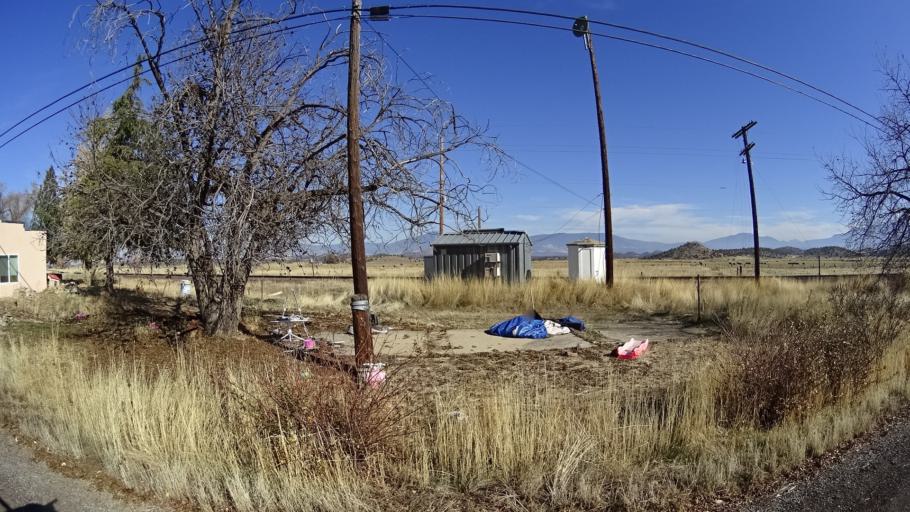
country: US
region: California
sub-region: Siskiyou County
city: Montague
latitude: 41.6386
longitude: -122.5217
